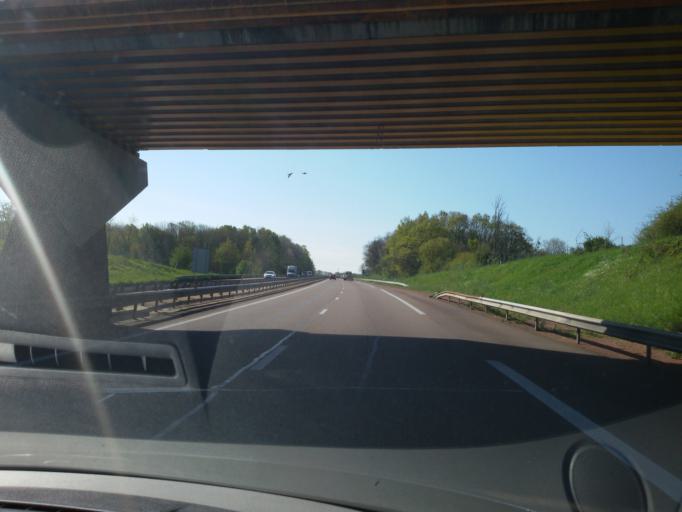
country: FR
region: Bourgogne
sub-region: Departement de l'Yonne
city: Venoy
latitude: 47.8141
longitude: 3.6250
